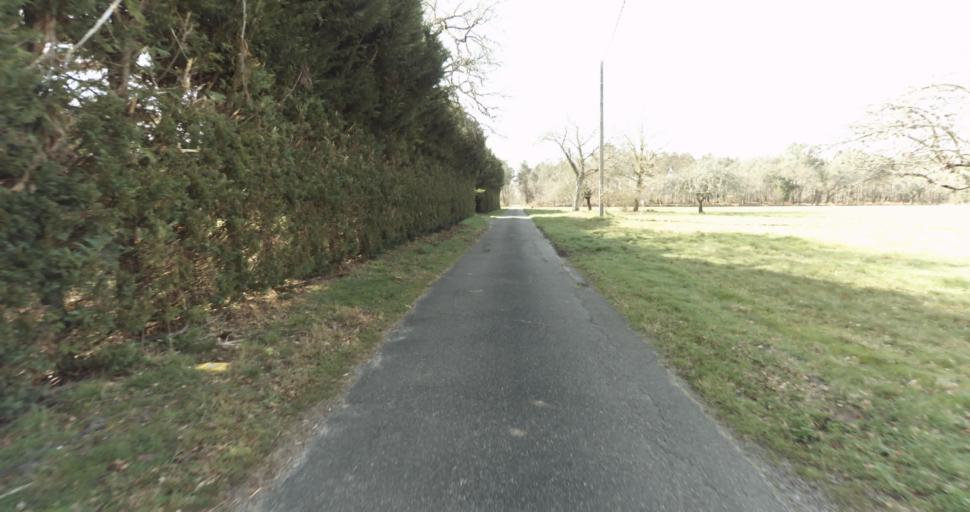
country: FR
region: Aquitaine
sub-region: Departement des Landes
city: Roquefort
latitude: 44.0766
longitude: -0.3557
